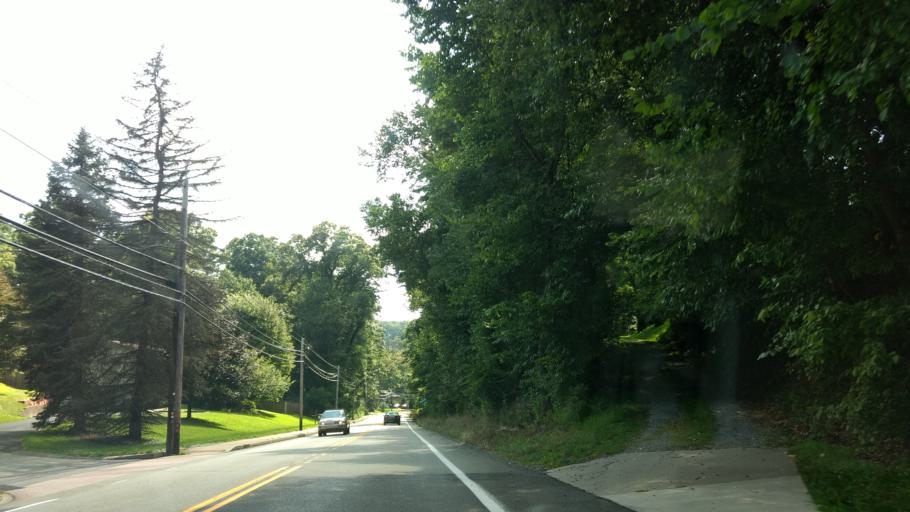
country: US
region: Pennsylvania
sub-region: Allegheny County
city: Bradford Woods
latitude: 40.6245
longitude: -80.0602
